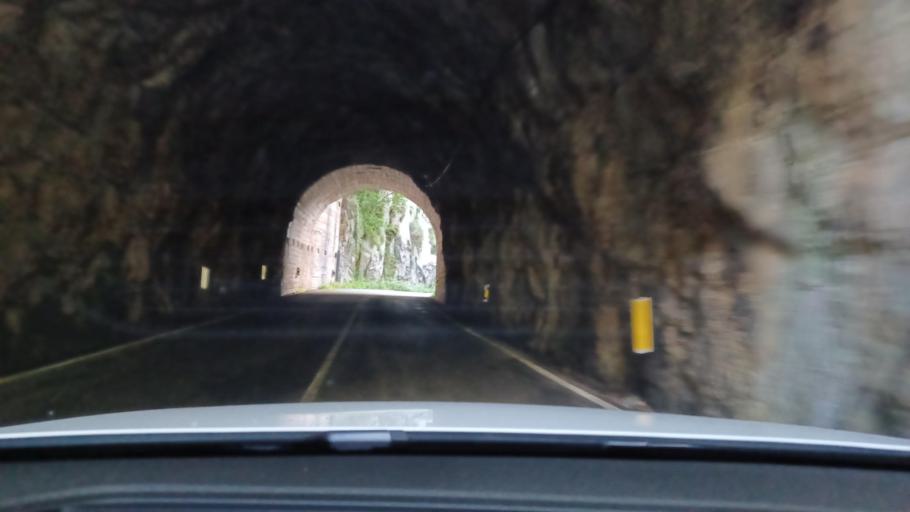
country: ES
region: Asturias
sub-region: Province of Asturias
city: La Plaza
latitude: 43.1193
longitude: -6.0517
